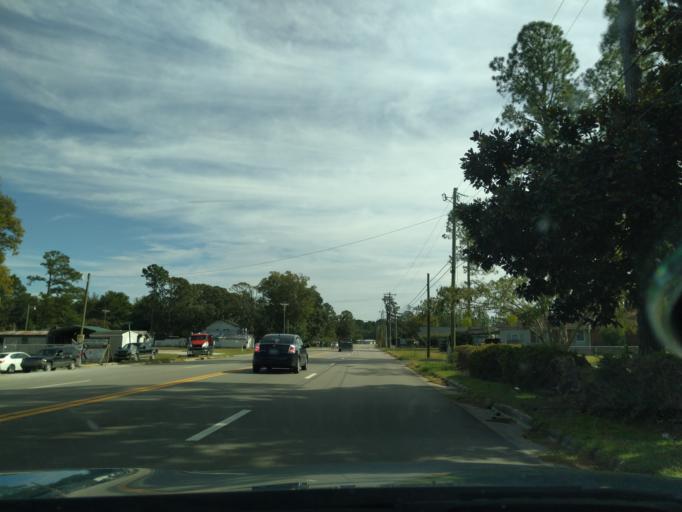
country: US
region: North Carolina
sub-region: Beaufort County
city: River Road
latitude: 35.5222
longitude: -77.0081
